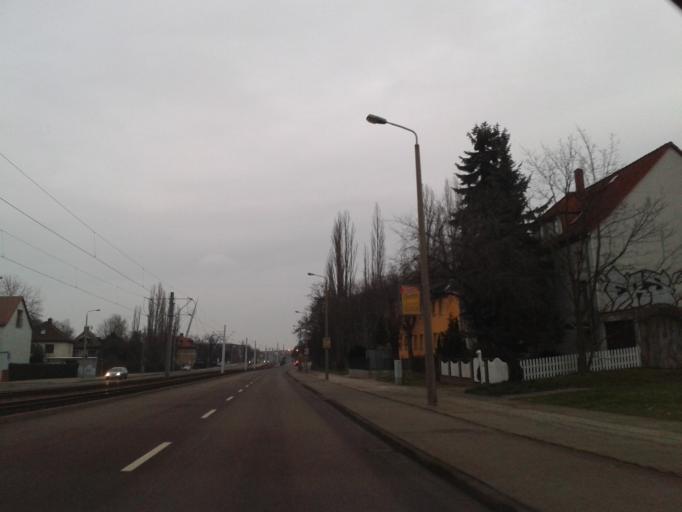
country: DE
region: Saxony-Anhalt
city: Halle Neustadt
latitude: 51.4567
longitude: 11.9444
